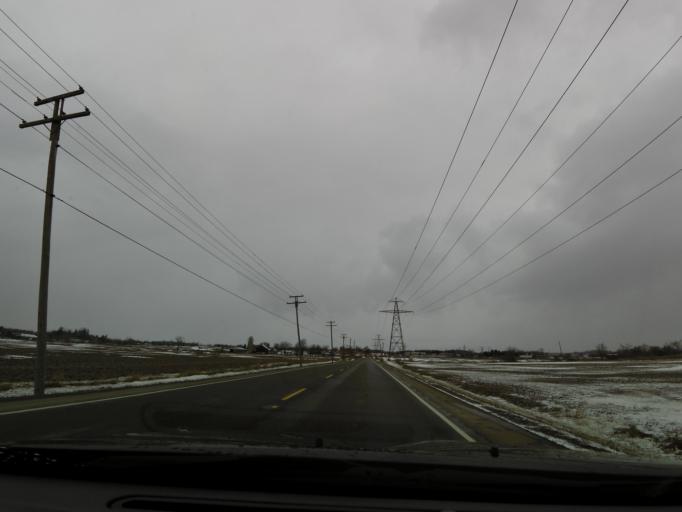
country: CA
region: Ontario
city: Ancaster
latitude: 43.2977
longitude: -79.9489
